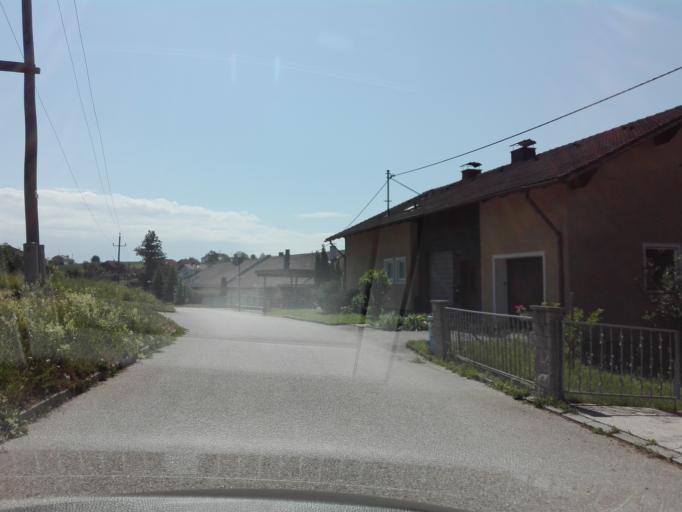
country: AT
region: Upper Austria
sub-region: Politischer Bezirk Urfahr-Umgebung
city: Engerwitzdorf
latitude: 48.2835
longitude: 14.4731
